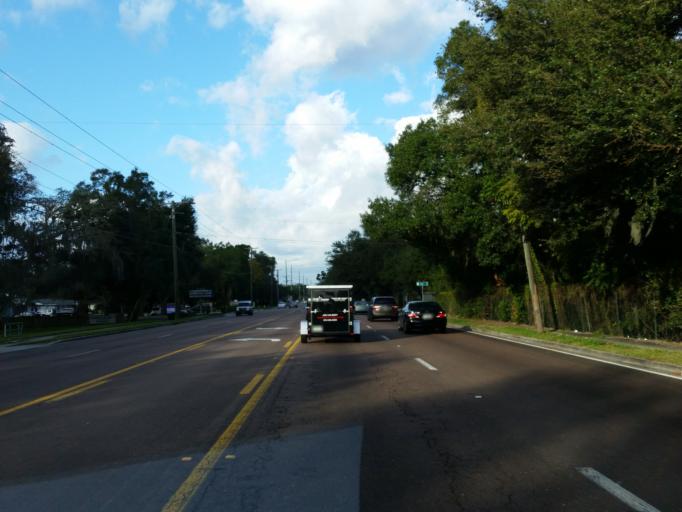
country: US
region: Florida
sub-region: Hillsborough County
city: Brandon
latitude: 27.8937
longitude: -82.2901
